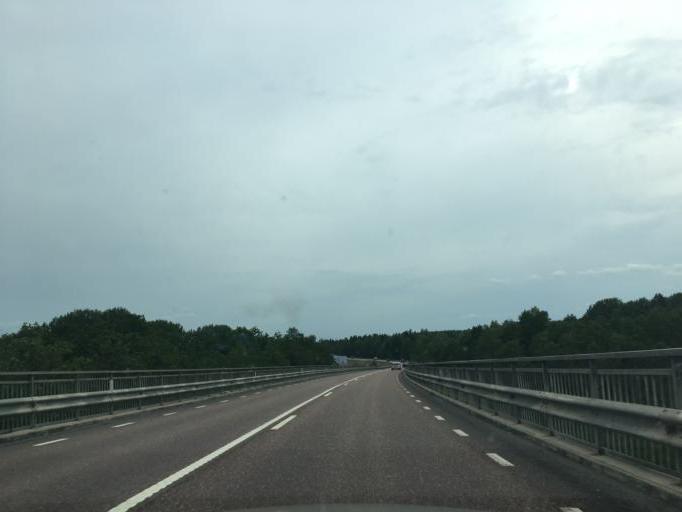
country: SE
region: Soedermanland
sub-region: Strangnas Kommun
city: Strangnas
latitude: 59.3937
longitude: 17.0037
